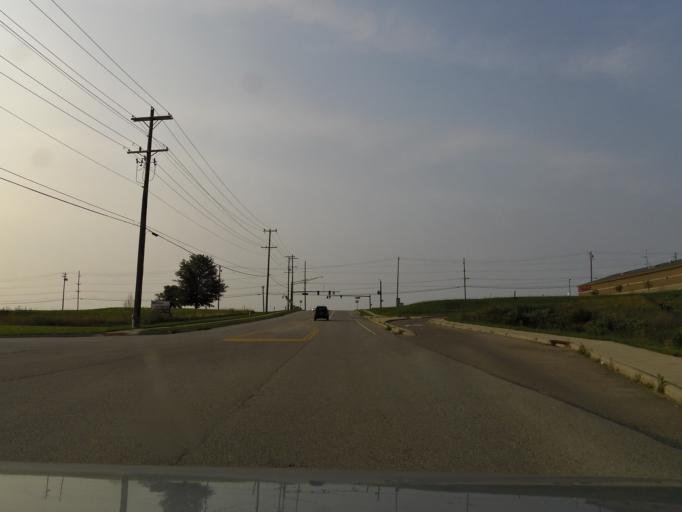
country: US
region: Ohio
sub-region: Butler County
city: Hamilton
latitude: 39.3897
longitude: -84.5150
